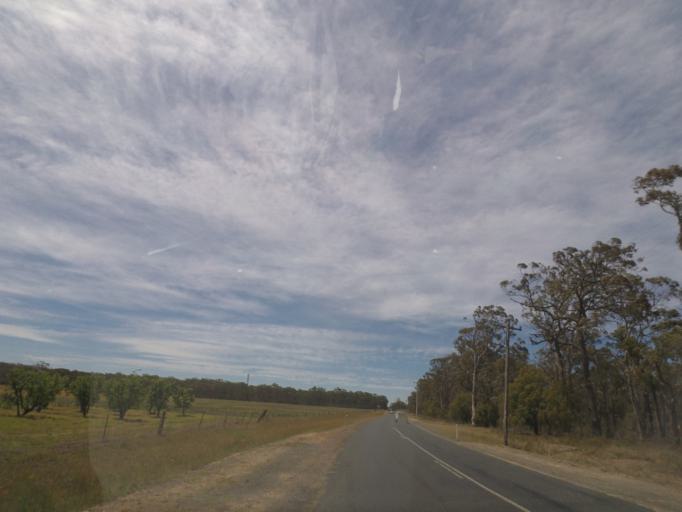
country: AU
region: New South Wales
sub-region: Wingecarribee
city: Colo Vale
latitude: -34.3479
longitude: 150.5546
